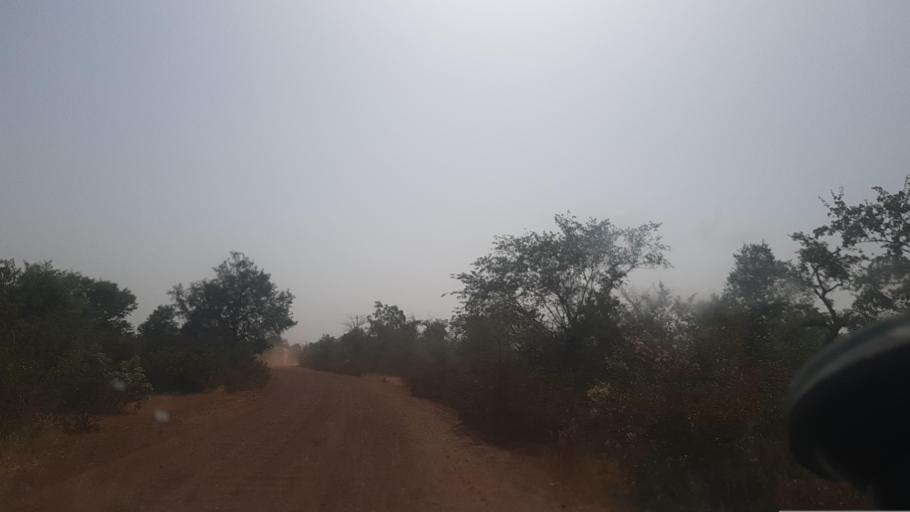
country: ML
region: Segou
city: Baroueli
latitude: 13.0749
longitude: -6.4824
